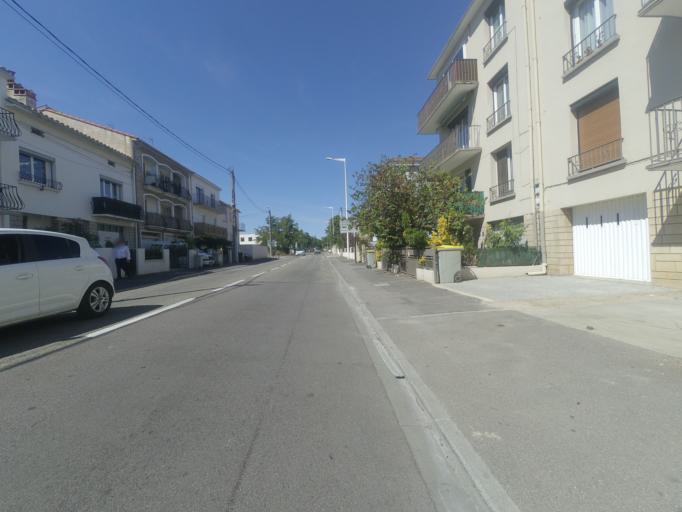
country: FR
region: Languedoc-Roussillon
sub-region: Departement des Pyrenees-Orientales
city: Perpignan
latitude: 42.6886
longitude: 2.9074
